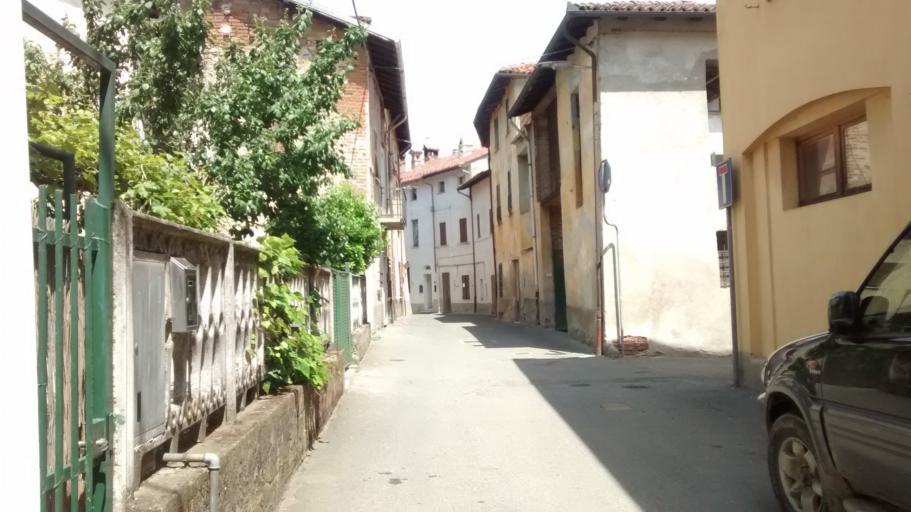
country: IT
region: Piedmont
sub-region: Provincia di Alessandria
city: Capriata d'Orba
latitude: 44.7310
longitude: 8.6898
